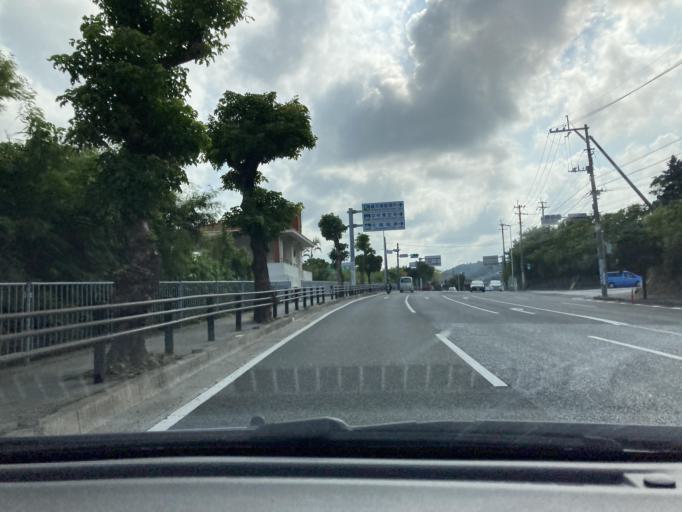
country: JP
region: Okinawa
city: Ginowan
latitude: 26.2738
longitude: 127.7975
